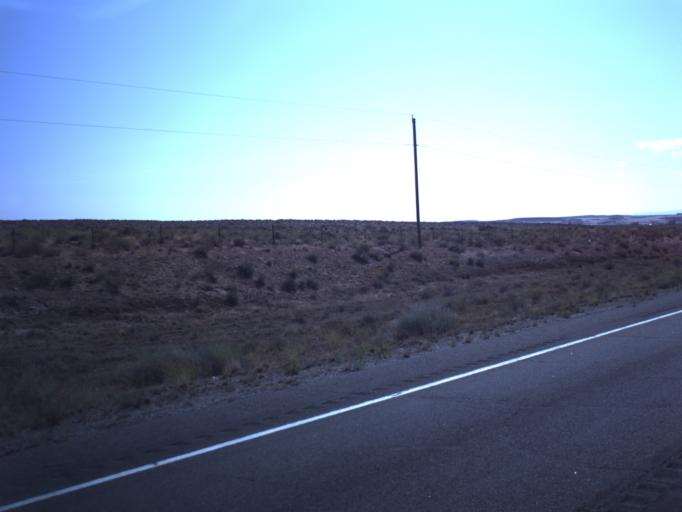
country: US
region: Utah
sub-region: San Juan County
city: Blanding
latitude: 37.1294
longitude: -109.5499
